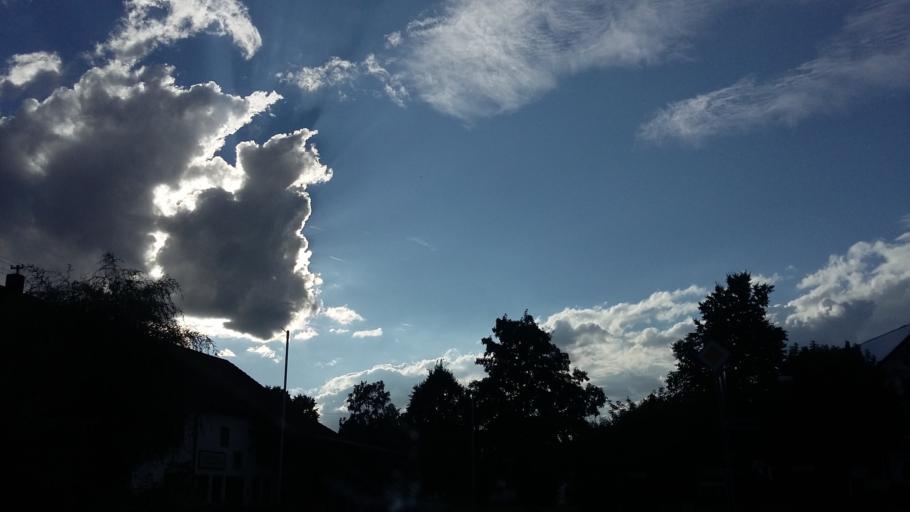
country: DE
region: Bavaria
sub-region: Upper Bavaria
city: Mittelstetten
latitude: 48.2546
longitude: 11.0966
